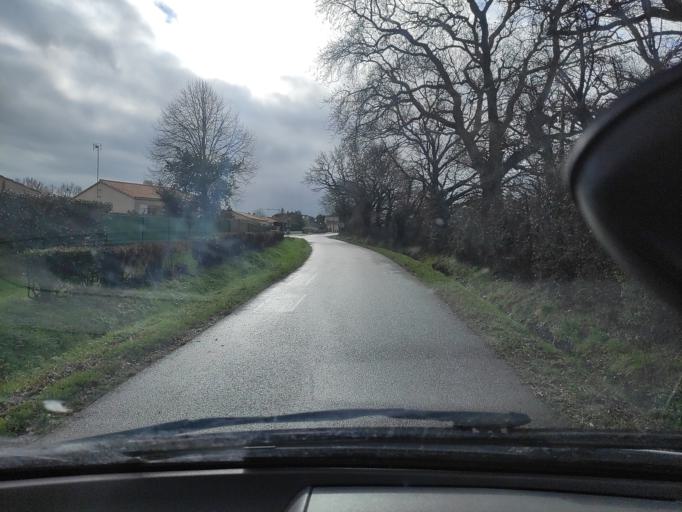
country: FR
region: Pays de la Loire
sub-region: Departement de la Vendee
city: La Boissiere-des-Landes
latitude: 46.5672
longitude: -1.4584
